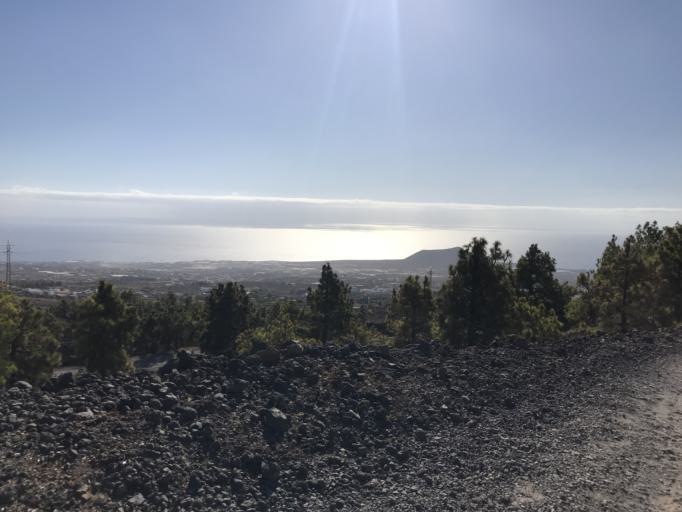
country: ES
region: Canary Islands
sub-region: Provincia de Santa Cruz de Tenerife
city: Arafo
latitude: 28.3302
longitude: -16.4255
